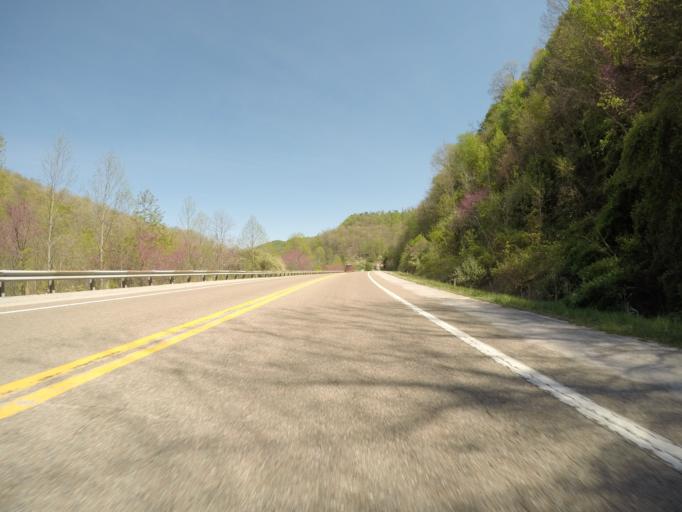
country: US
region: West Virginia
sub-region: Kanawha County
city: Charleston
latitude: 38.4132
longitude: -81.6365
